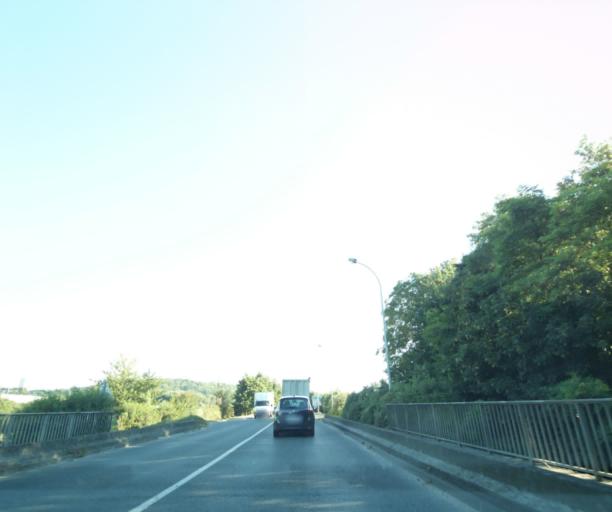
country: FR
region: Ile-de-France
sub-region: Departement de Seine-et-Marne
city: Montereau-Fault-Yonne
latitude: 48.3819
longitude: 2.9653
